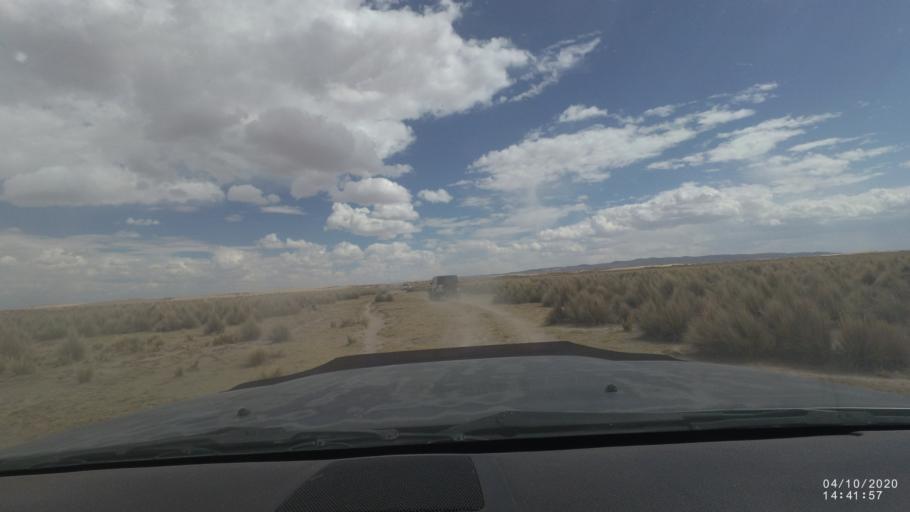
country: BO
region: Oruro
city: Poopo
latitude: -18.6844
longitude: -67.4909
